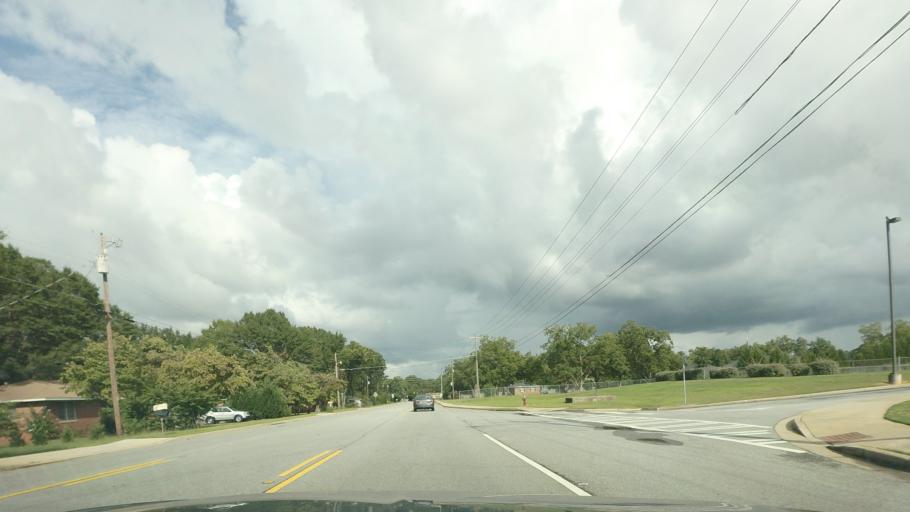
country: US
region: Georgia
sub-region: Houston County
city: Centerville
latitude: 32.6348
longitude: -83.6931
